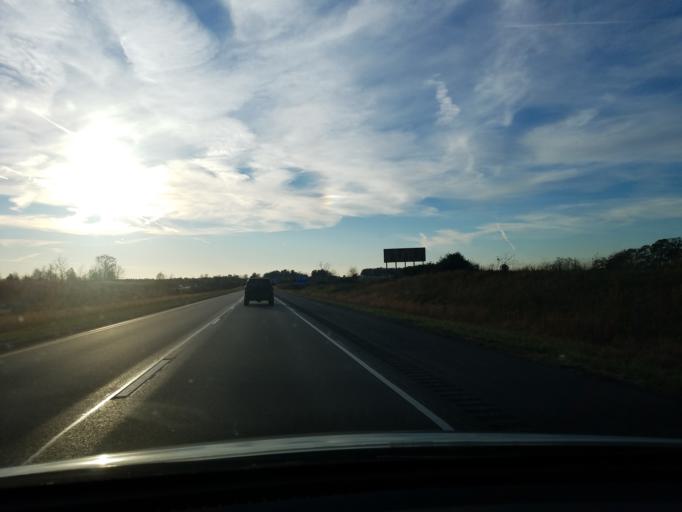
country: US
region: Indiana
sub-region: Spencer County
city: Dale
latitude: 38.1985
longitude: -86.9335
